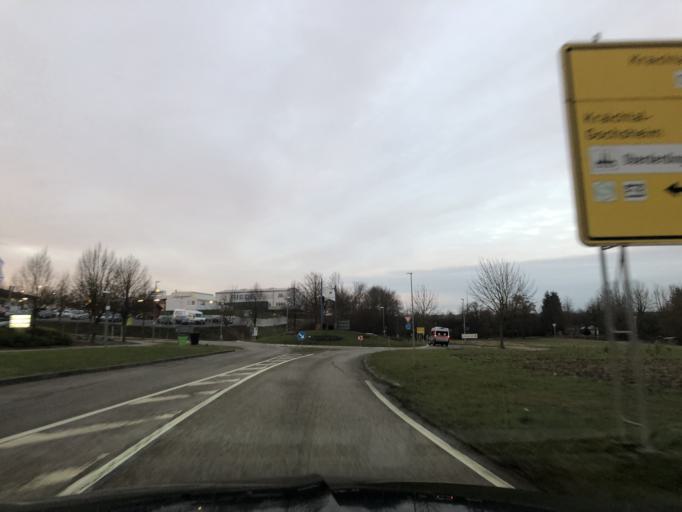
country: DE
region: Baden-Wuerttemberg
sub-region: Karlsruhe Region
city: Oberderdingen
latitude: 49.0815
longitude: 8.7802
